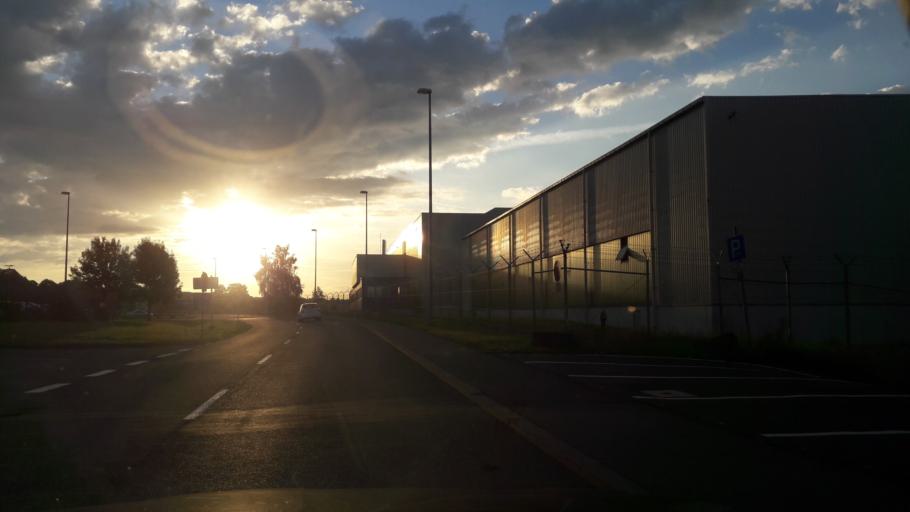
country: DE
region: Saarland
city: Sankt Ingbert
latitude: 49.2203
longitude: 7.1146
